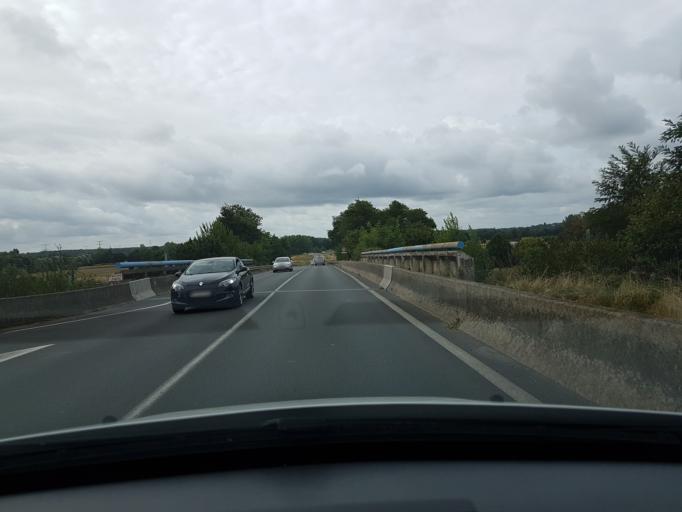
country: FR
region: Centre
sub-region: Departement d'Indre-et-Loire
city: La Ville-aux-Dames
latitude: 47.3892
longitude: 0.7870
